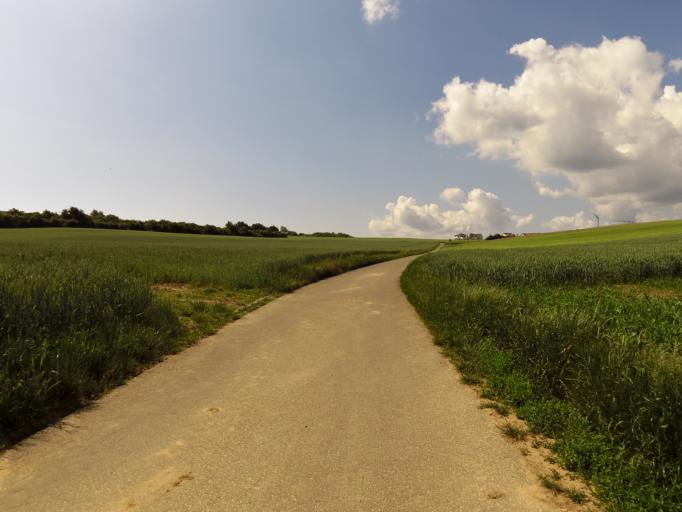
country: DE
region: Rheinland-Pfalz
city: Tiefenthal
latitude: 49.5462
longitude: 8.1123
